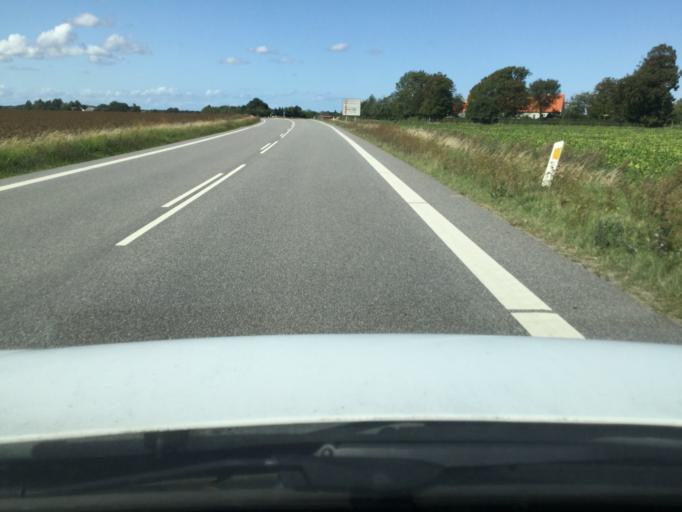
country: DK
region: Zealand
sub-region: Lolland Kommune
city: Rodby
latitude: 54.7440
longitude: 11.3881
